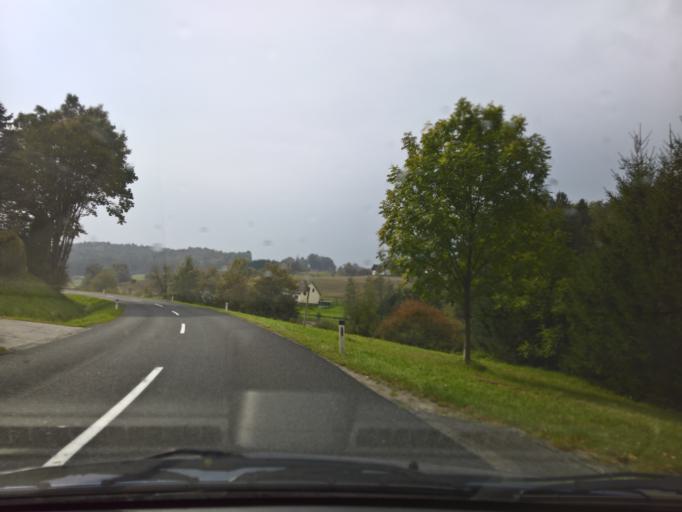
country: AT
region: Styria
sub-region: Politischer Bezirk Deutschlandsberg
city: Unterbergla
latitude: 46.7826
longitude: 15.3395
